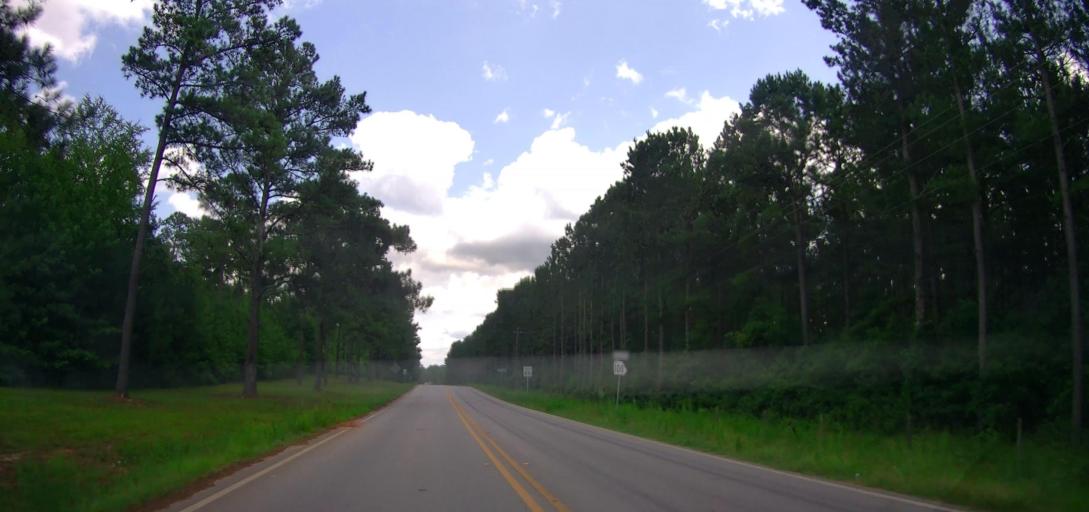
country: US
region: Georgia
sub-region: Troup County
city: Hogansville
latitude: 33.1587
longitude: -84.8619
